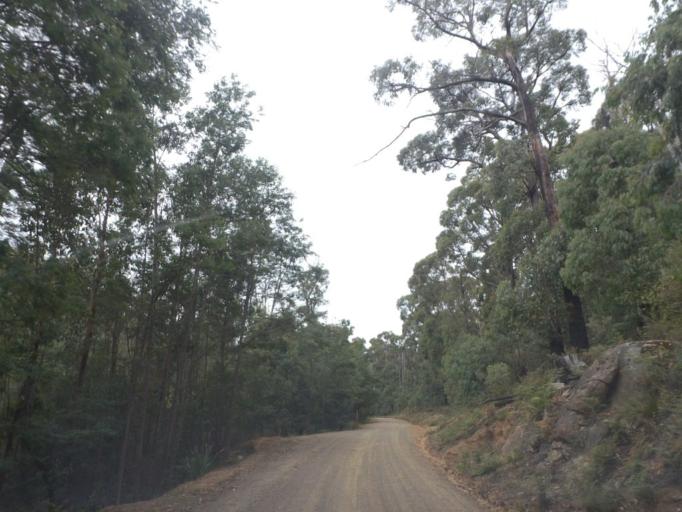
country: AU
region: Victoria
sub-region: Yarra Ranges
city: Healesville
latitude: -37.4235
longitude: 145.5829
